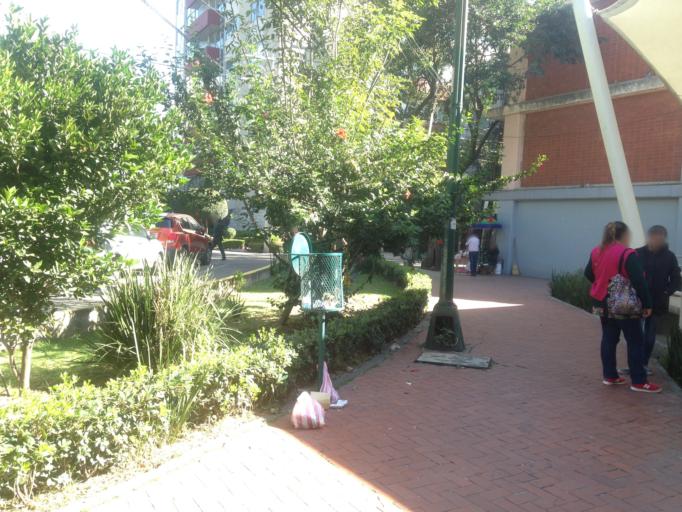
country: MX
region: Mexico City
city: Colonia del Valle
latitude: 19.3851
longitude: -99.1692
